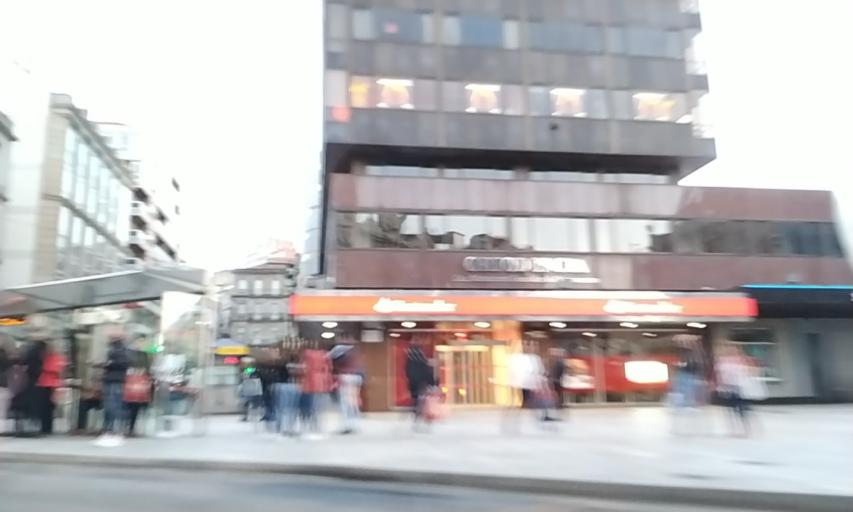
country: ES
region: Galicia
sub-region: Provincia de Pontevedra
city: Vigo
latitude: 42.2360
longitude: -8.7201
